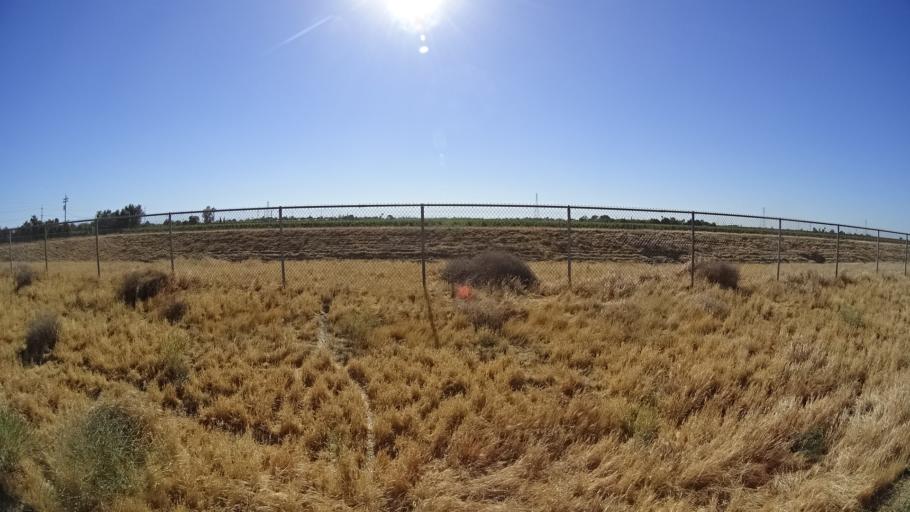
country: US
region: California
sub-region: Fresno County
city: West Park
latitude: 36.7048
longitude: -119.8270
